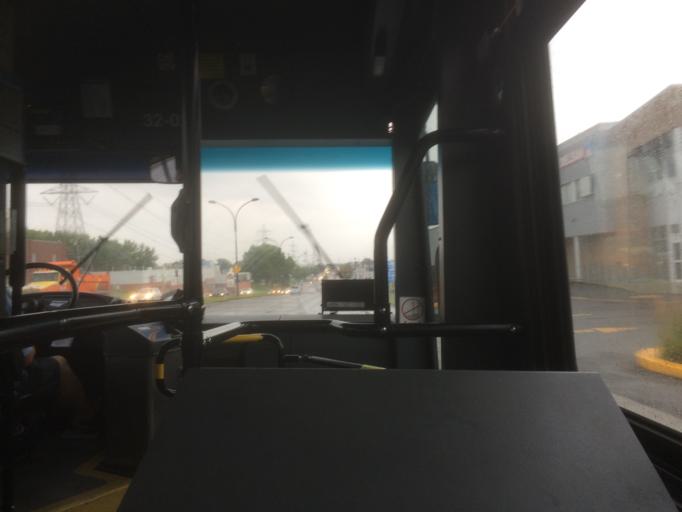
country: CA
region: Quebec
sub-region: Montreal
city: Saint-Leonard
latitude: 45.6235
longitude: -73.5845
